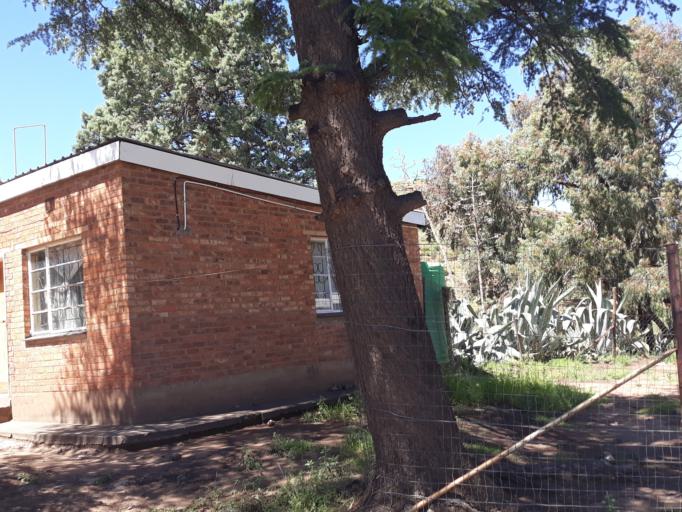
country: LS
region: Quthing
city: Quthing
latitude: -30.3444
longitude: 27.5425
